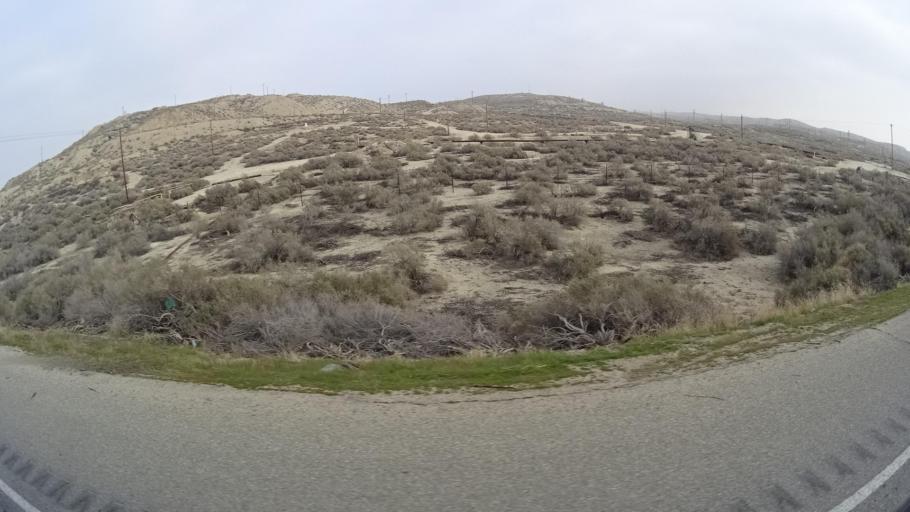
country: US
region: California
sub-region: Kern County
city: Ford City
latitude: 35.1823
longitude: -119.4543
